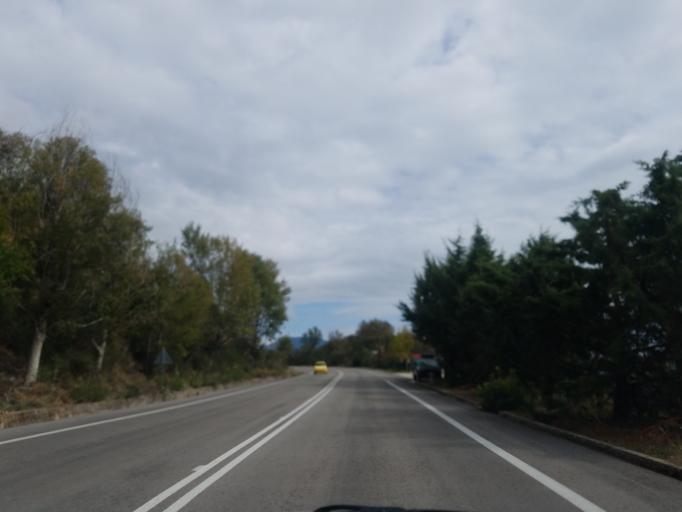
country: GR
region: Central Greece
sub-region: Nomos Voiotias
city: Arachova
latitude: 38.4859
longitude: 22.5589
